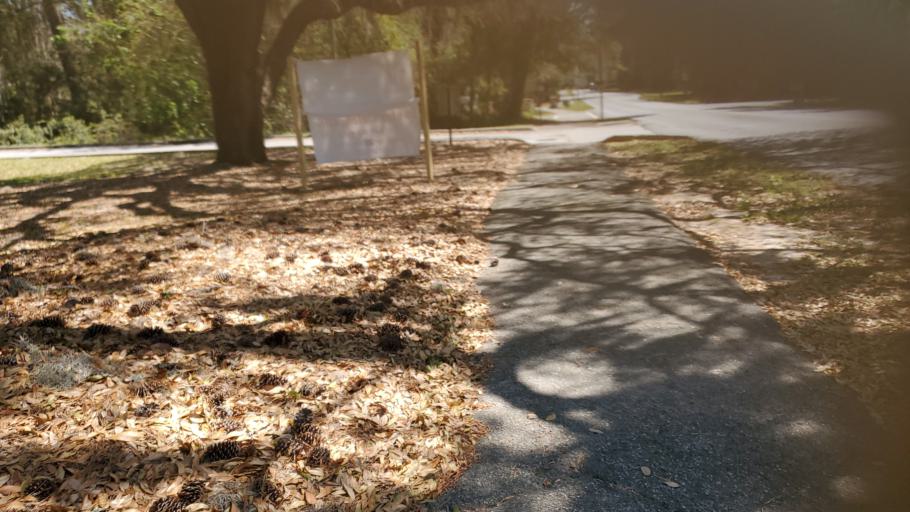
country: US
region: Georgia
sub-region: Chatham County
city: Wilmington Island
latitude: 32.0058
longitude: -80.9878
